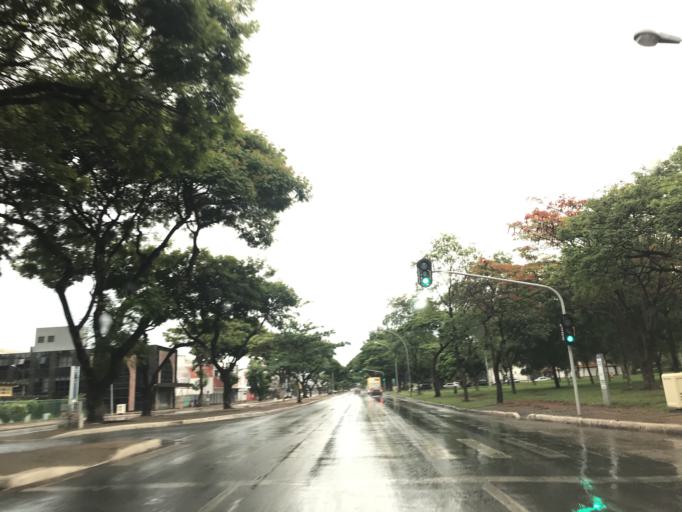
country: BR
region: Federal District
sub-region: Brasilia
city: Brasilia
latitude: -15.8251
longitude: -47.9238
